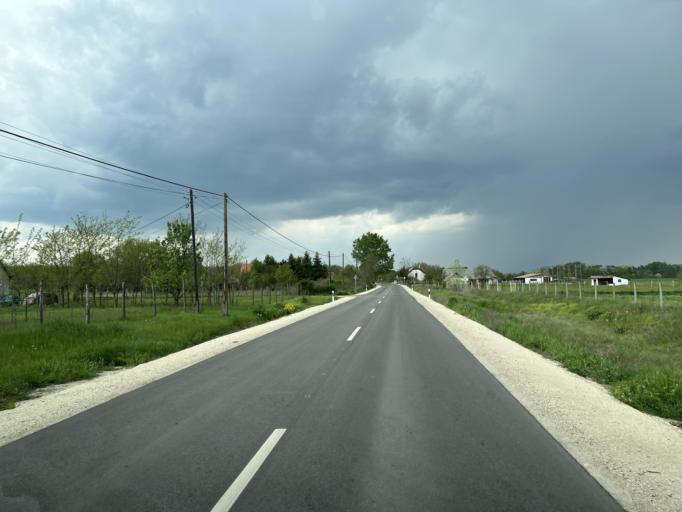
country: HU
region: Pest
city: Nagykoros
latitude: 47.0392
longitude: 19.7493
